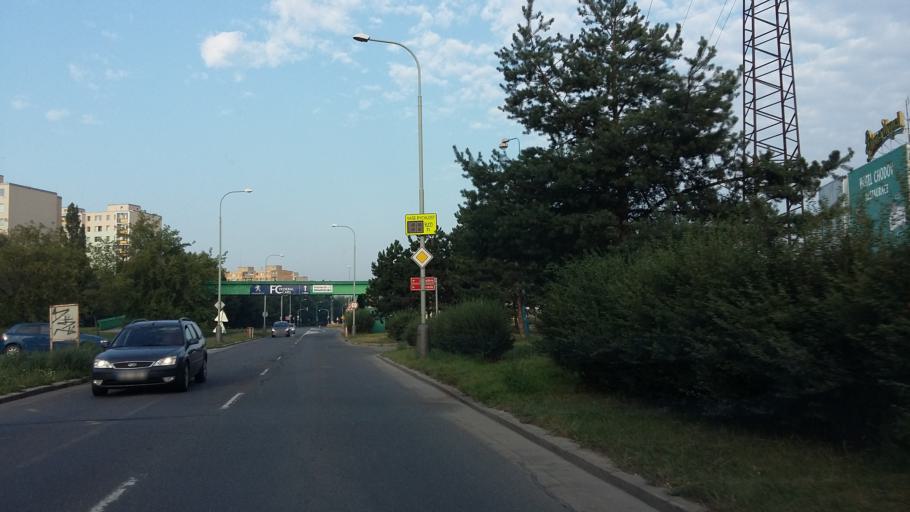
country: CZ
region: Central Bohemia
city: Vestec
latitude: 50.0399
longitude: 14.5065
